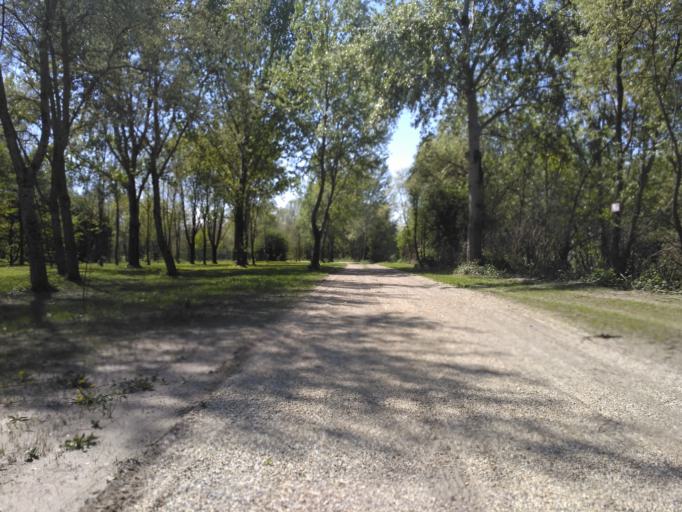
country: IT
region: Piedmont
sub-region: Provincia di Cuneo
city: Faule
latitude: 44.8171
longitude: 7.5747
